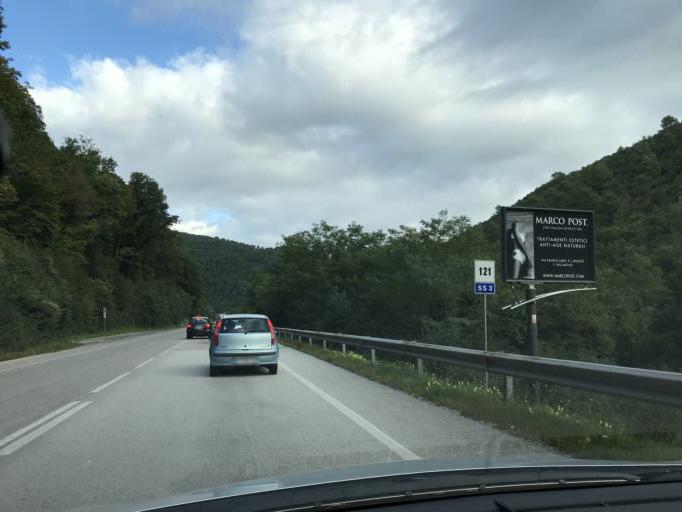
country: IT
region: Umbria
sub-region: Provincia di Perugia
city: Spoleto
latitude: 42.7024
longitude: 12.7226
